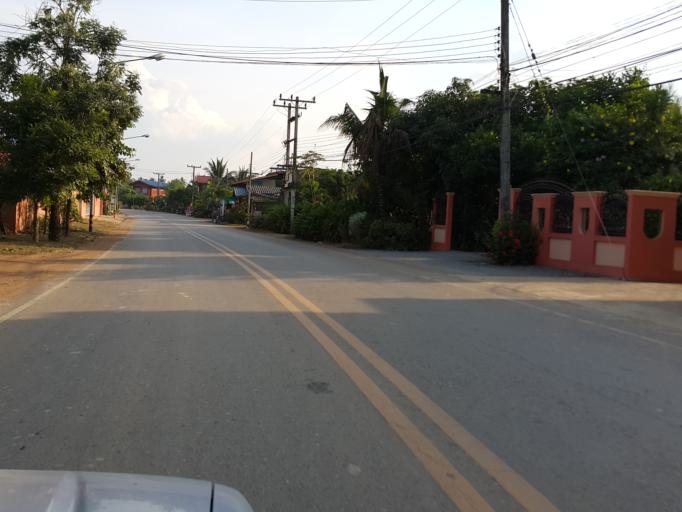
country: TH
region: Sukhothai
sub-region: Amphoe Si Satchanalai
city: Si Satchanalai
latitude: 17.4330
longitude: 99.6882
